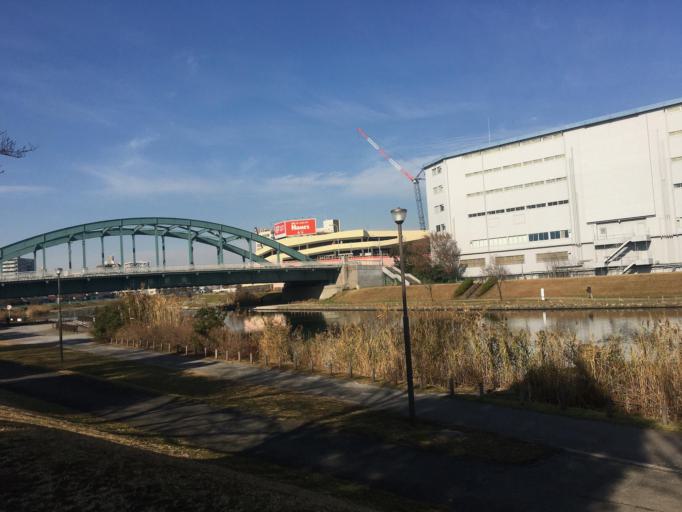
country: JP
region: Tokyo
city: Urayasu
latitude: 35.7020
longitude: 139.8365
